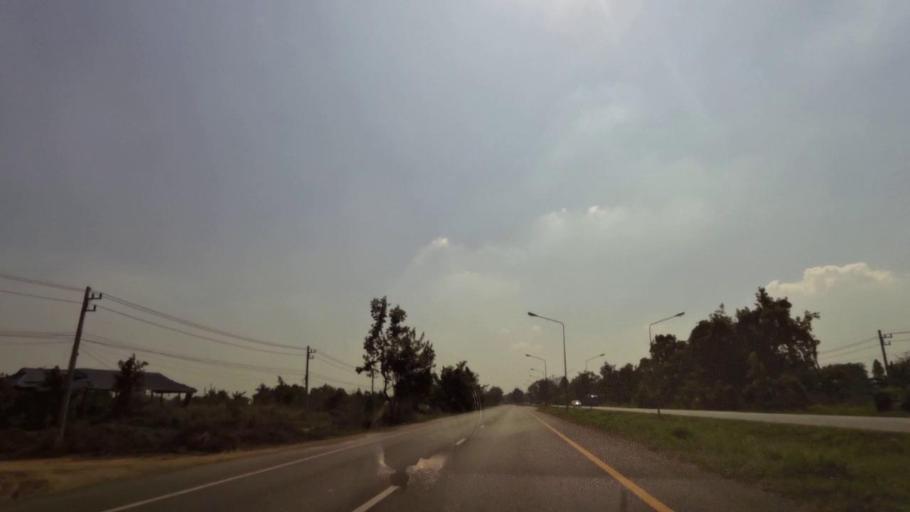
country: TH
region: Phichit
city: Bueng Na Rang
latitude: 16.2448
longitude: 100.1255
